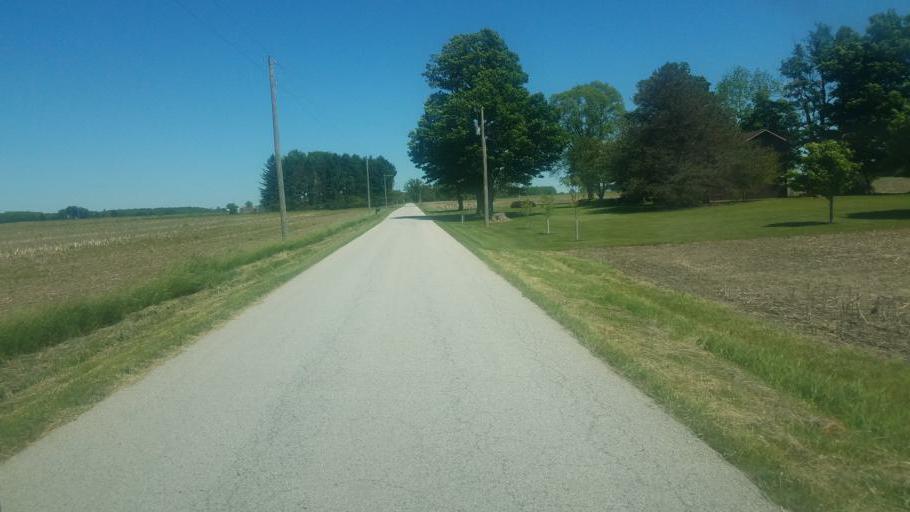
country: US
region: Ohio
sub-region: Champaign County
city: Saint Paris
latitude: 40.1995
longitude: -84.0462
